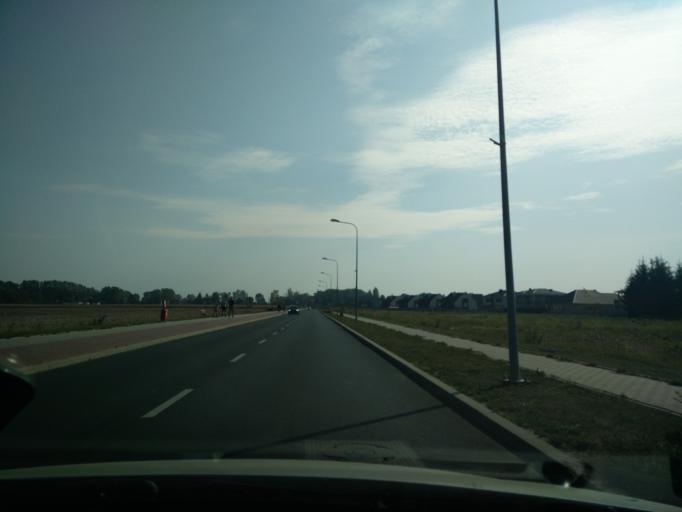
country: PL
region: Greater Poland Voivodeship
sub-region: Powiat sredzki
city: Sroda Wielkopolska
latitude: 52.2384
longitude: 17.2779
